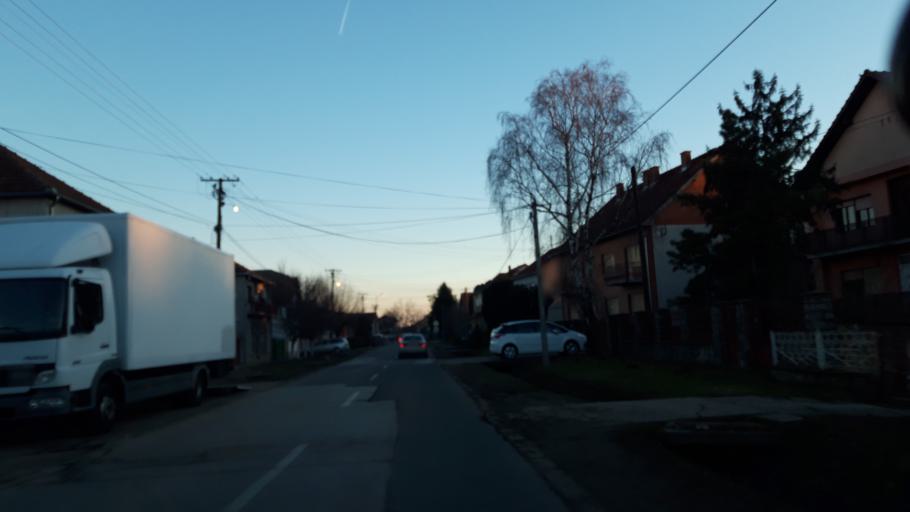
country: RS
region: Autonomna Pokrajina Vojvodina
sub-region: Sremski Okrug
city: Ingija
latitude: 45.0395
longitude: 20.0796
